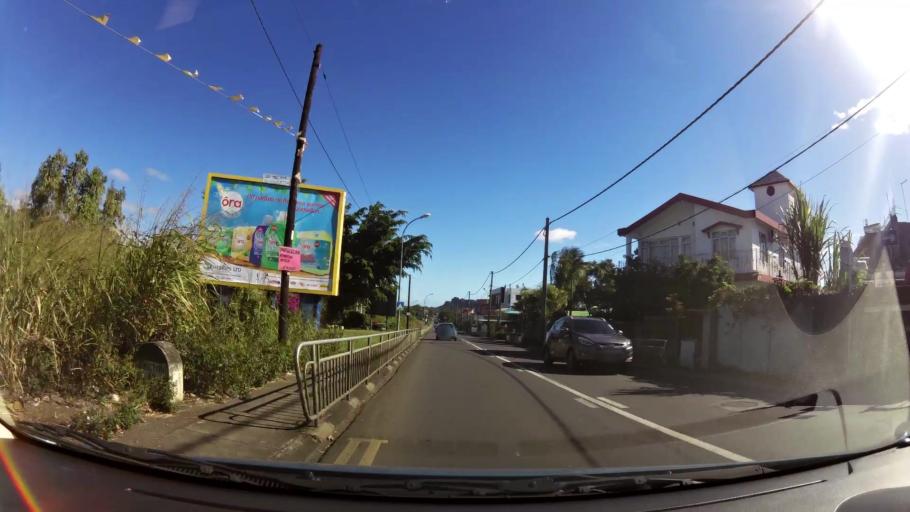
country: MU
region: Plaines Wilhems
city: Vacoas
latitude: -20.2810
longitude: 57.4542
